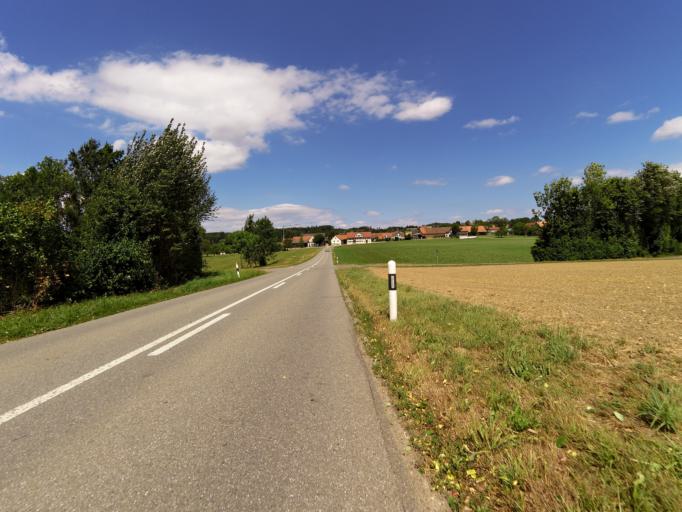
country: CH
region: Thurgau
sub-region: Weinfelden District
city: Maerstetten-Dorf
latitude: 47.6134
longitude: 9.0648
